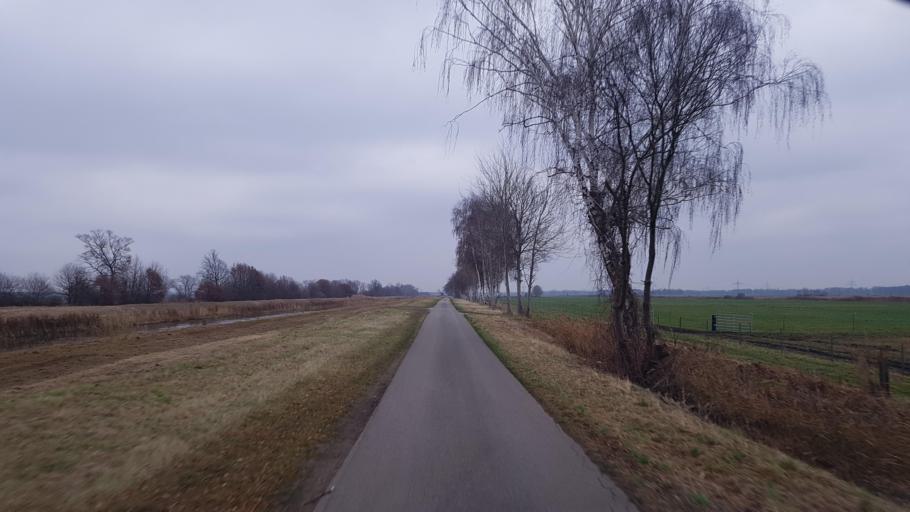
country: DE
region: Brandenburg
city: Plessa
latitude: 51.4630
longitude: 13.6415
